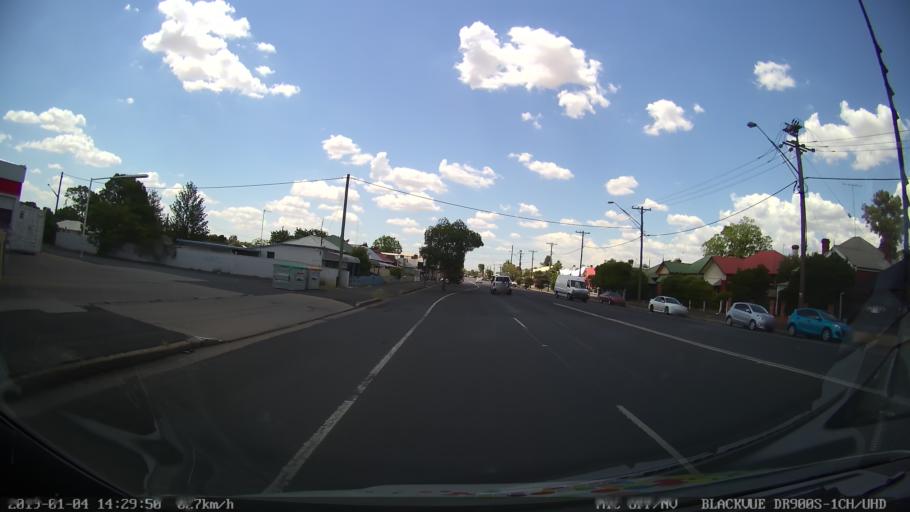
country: AU
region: New South Wales
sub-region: Dubbo Municipality
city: Dubbo
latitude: -32.2434
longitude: 148.6093
